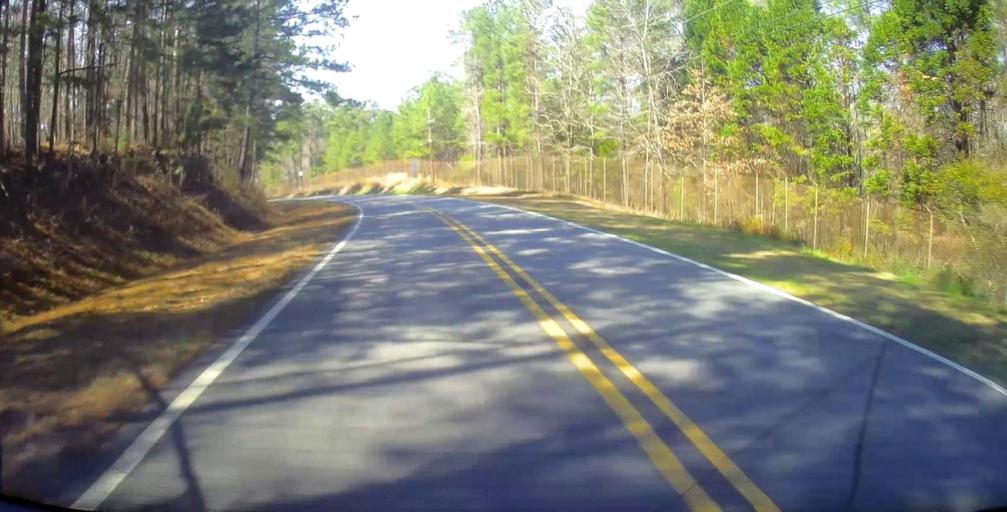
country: US
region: Georgia
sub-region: Bibb County
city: Macon
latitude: 32.9047
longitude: -83.6190
